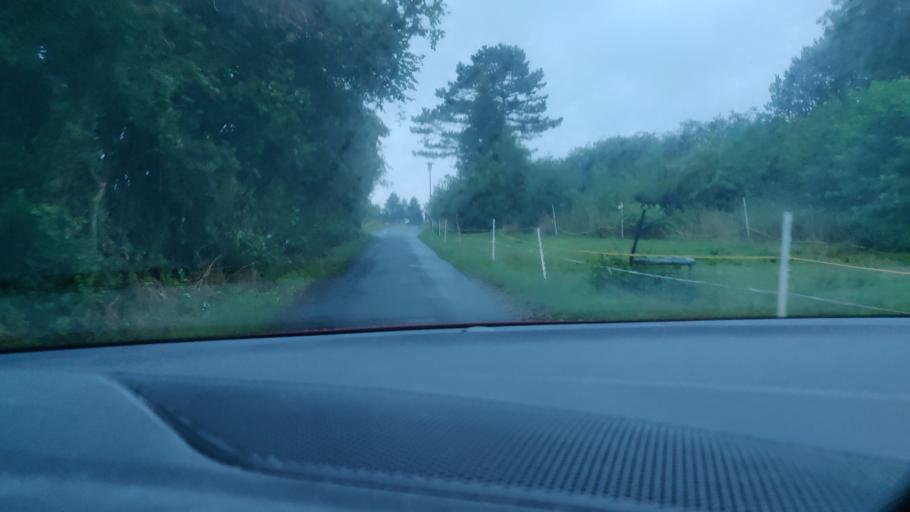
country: DE
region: Lower Saxony
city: Cuxhaven
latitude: 53.8682
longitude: 8.6457
